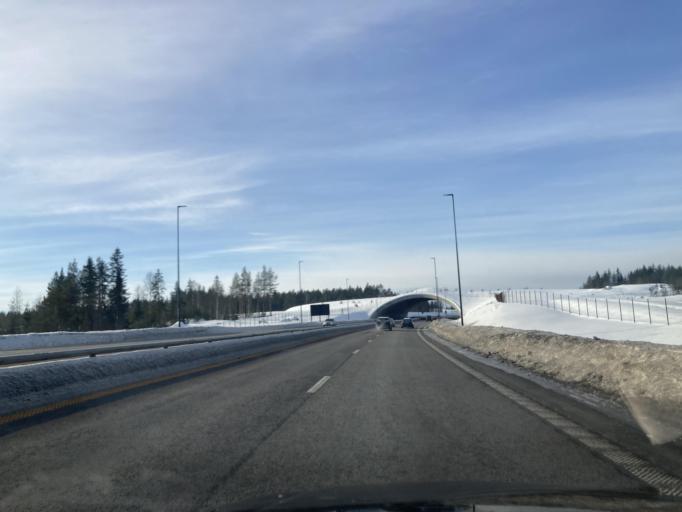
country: NO
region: Hedmark
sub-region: Elverum
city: Elverum
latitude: 60.8846
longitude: 11.5006
